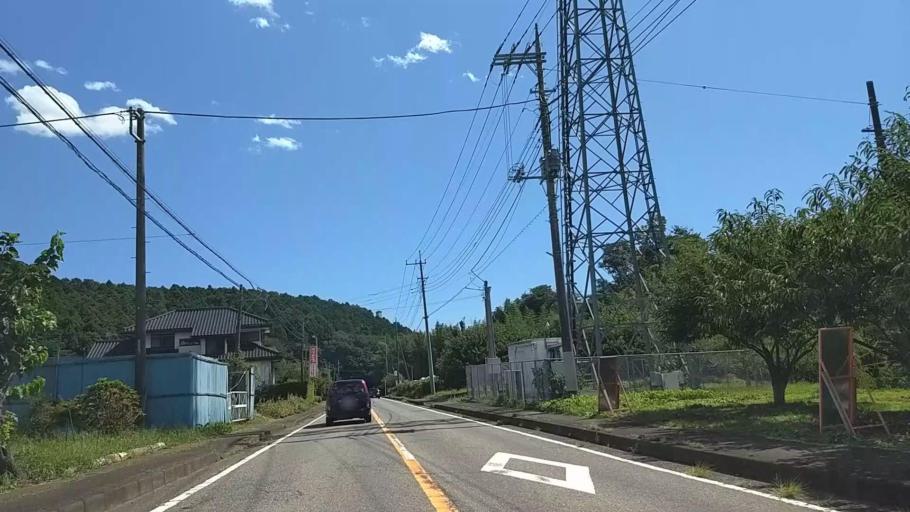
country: JP
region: Kanagawa
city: Zama
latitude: 35.5481
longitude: 139.2971
